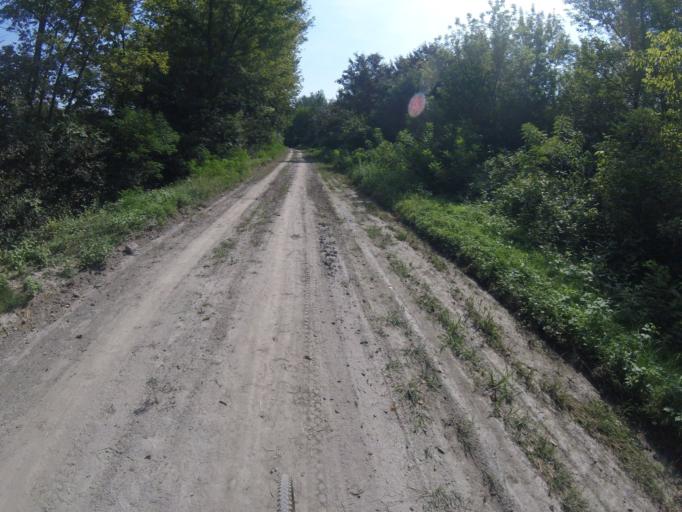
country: HU
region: Bacs-Kiskun
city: Baja
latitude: 46.1965
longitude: 18.9064
